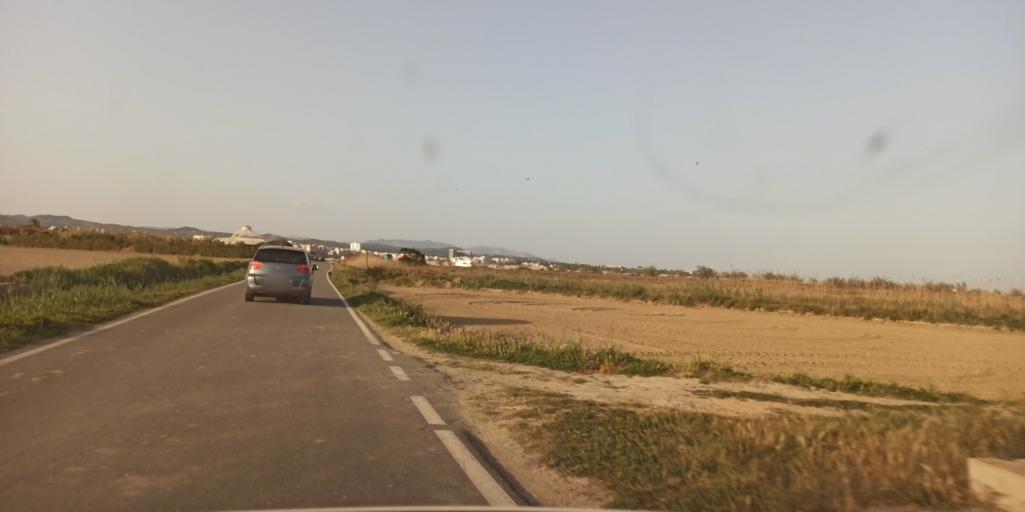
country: ES
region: Catalonia
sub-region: Provincia de Tarragona
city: L'Ampolla
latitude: 40.7949
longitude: 0.6994
